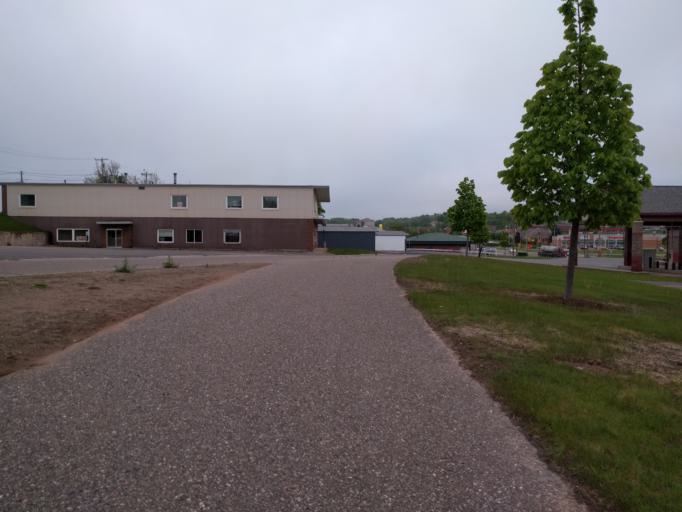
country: US
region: Michigan
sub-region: Marquette County
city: Trowbridge Park
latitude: 46.5478
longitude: -87.4187
